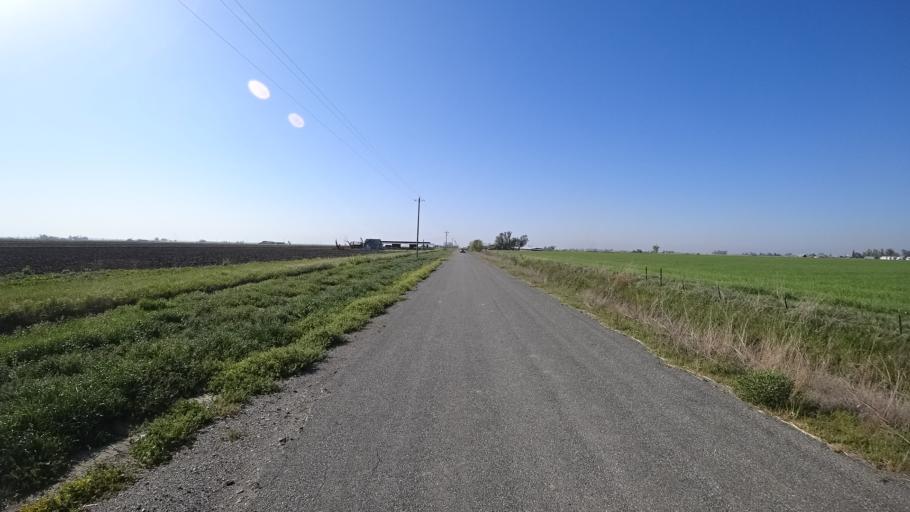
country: US
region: California
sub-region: Glenn County
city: Willows
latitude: 39.5797
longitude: -122.0839
